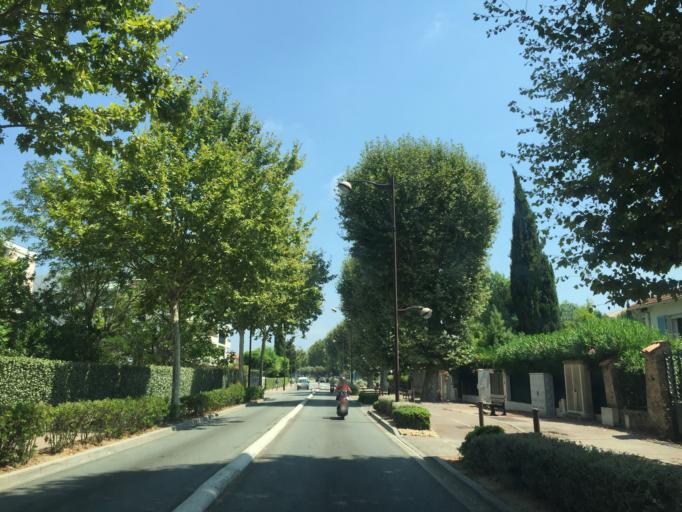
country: FR
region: Provence-Alpes-Cote d'Azur
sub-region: Departement du Var
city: Frejus
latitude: 43.4331
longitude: 6.7469
